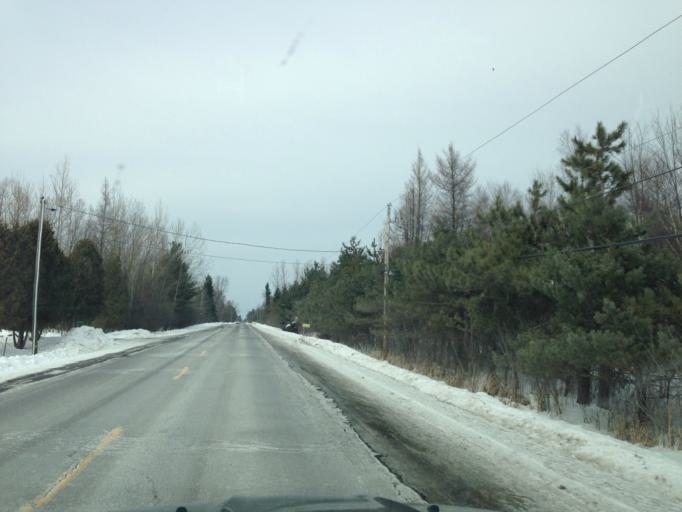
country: CA
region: Ontario
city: Ottawa
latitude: 45.3252
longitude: -75.5419
